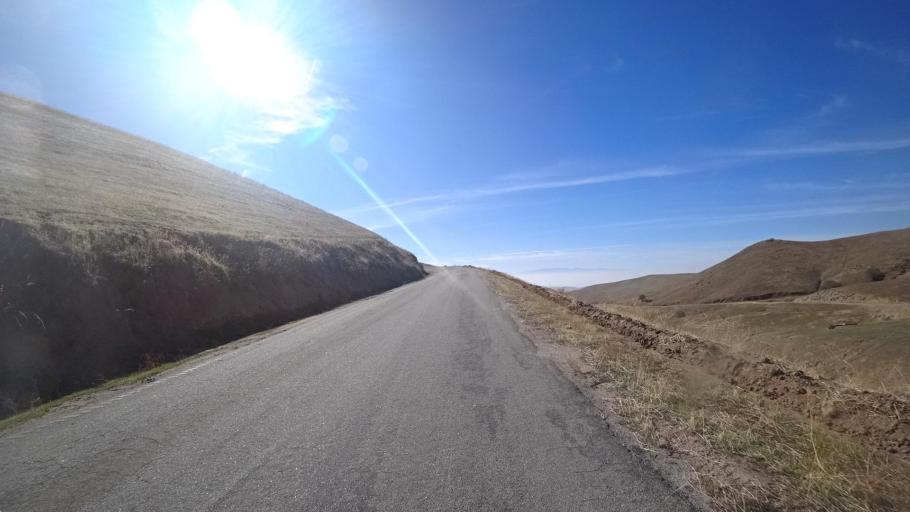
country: US
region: California
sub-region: Kern County
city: Arvin
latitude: 35.4222
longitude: -118.7405
